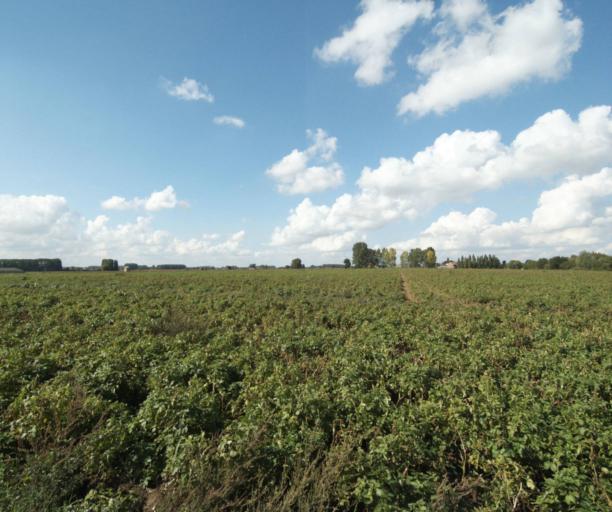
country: FR
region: Nord-Pas-de-Calais
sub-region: Departement du Nord
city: Illies
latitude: 50.5694
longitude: 2.8321
